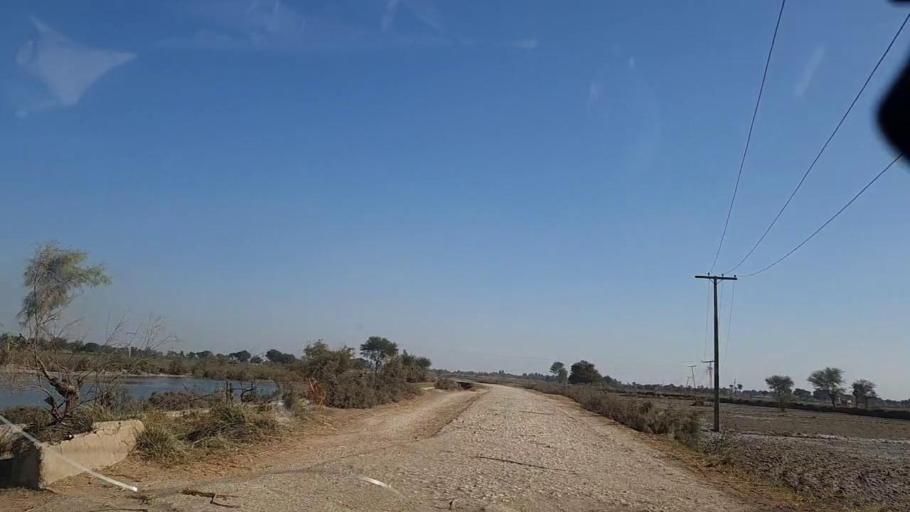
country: PK
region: Sindh
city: Khanpur
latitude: 27.8035
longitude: 69.3713
